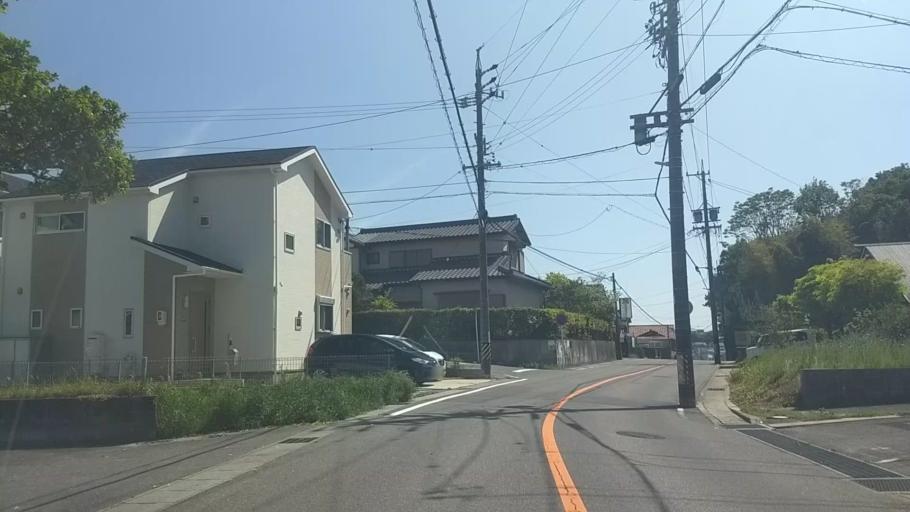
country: JP
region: Aichi
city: Okazaki
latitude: 34.9704
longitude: 137.1791
